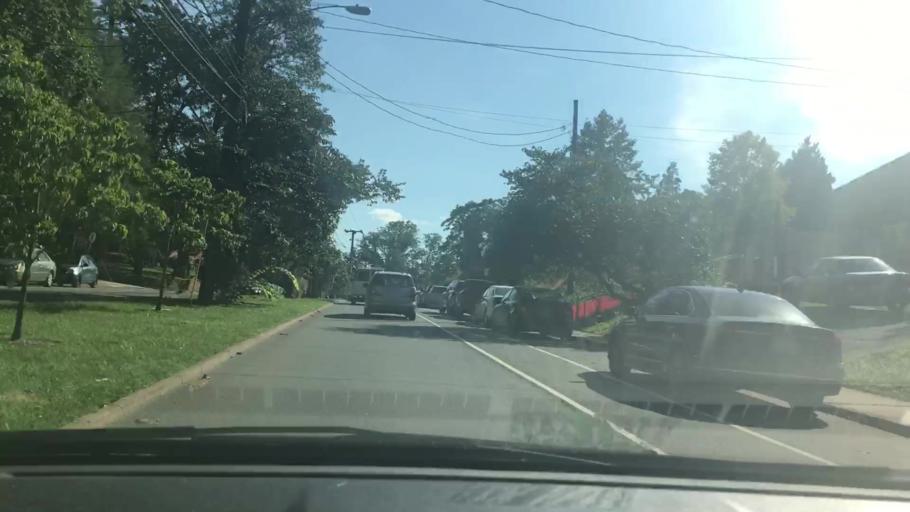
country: US
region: Virginia
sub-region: City of Charlottesville
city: Charlottesville
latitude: 38.0298
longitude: -78.5091
